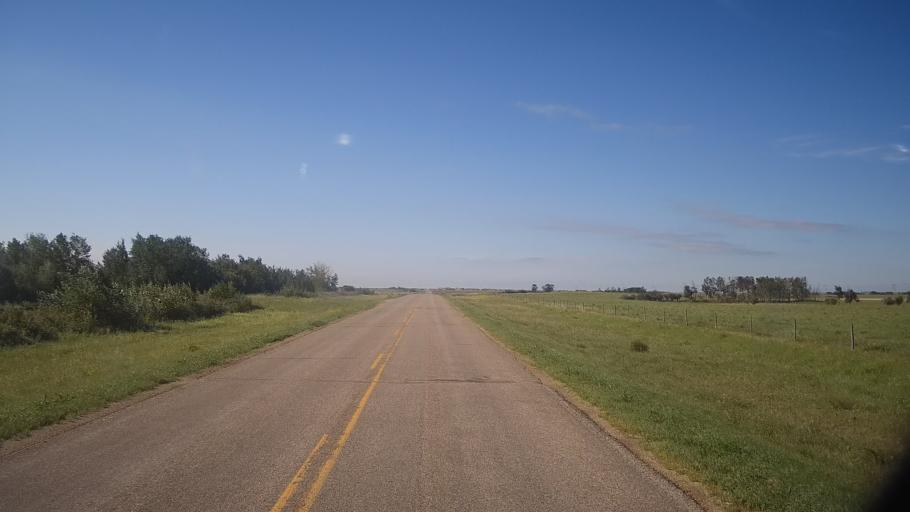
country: CA
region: Saskatchewan
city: Watrous
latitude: 51.7492
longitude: -105.2867
